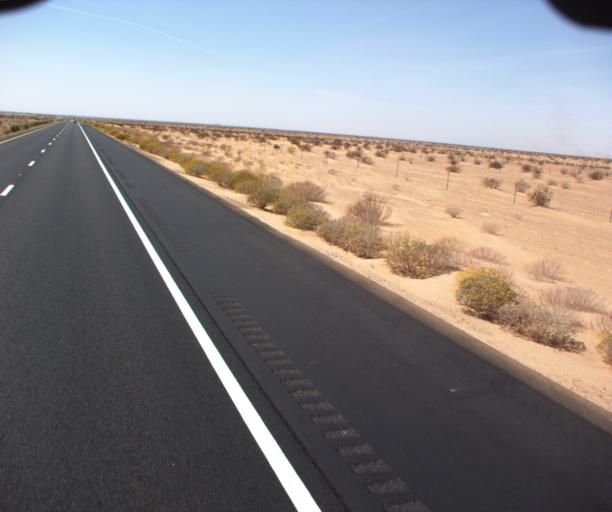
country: US
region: Arizona
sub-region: Yuma County
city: Somerton
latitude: 32.4954
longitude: -114.5925
